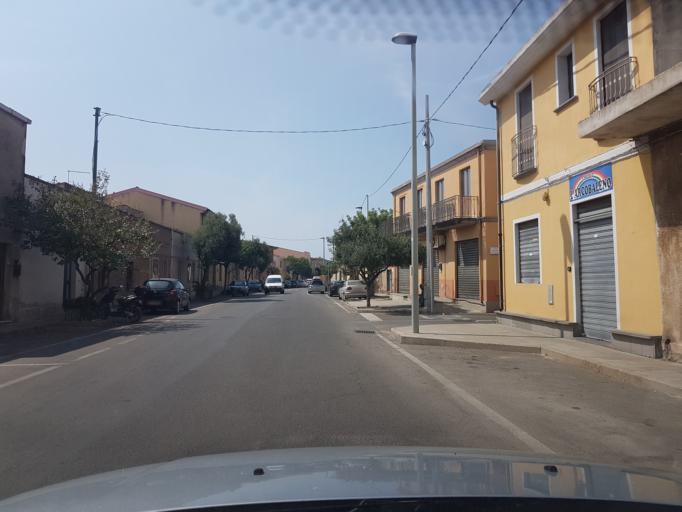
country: IT
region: Sardinia
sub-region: Provincia di Oristano
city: Cabras
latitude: 39.9258
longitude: 8.5357
